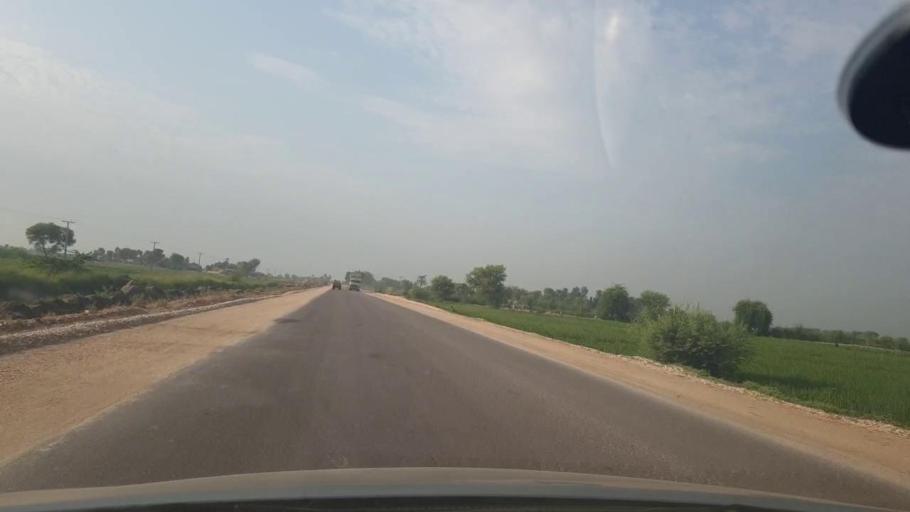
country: PK
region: Sindh
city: Jacobabad
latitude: 28.2033
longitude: 68.3680
